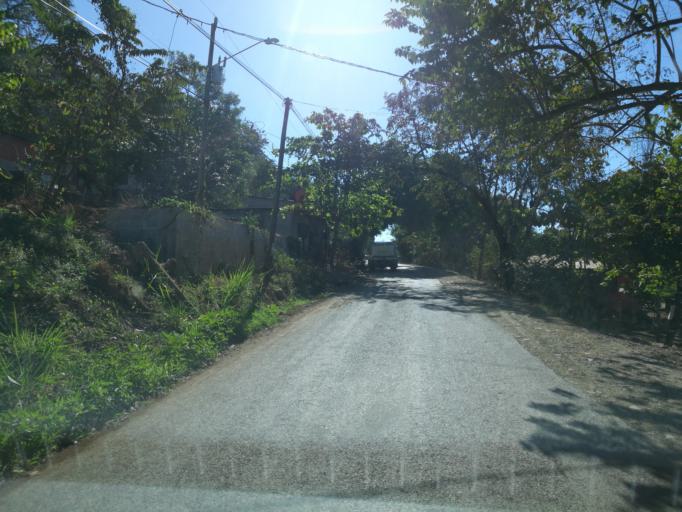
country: CR
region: Guanacaste
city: Juntas
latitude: 10.1030
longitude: -84.9985
